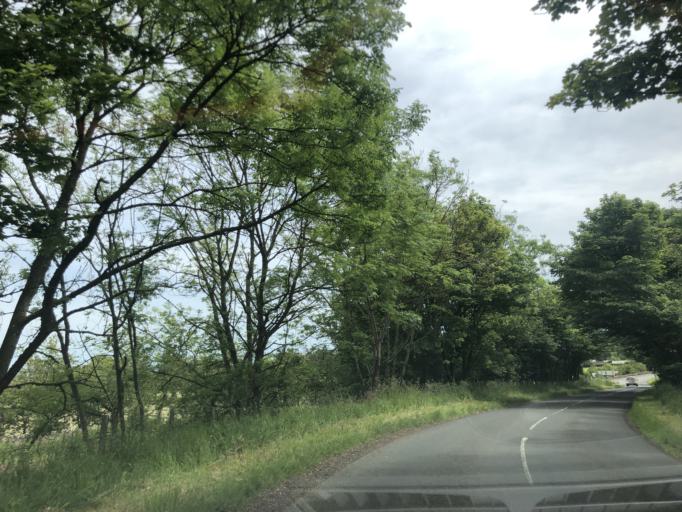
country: GB
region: Scotland
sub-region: Fife
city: Anstruther
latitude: 56.2657
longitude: -2.6358
